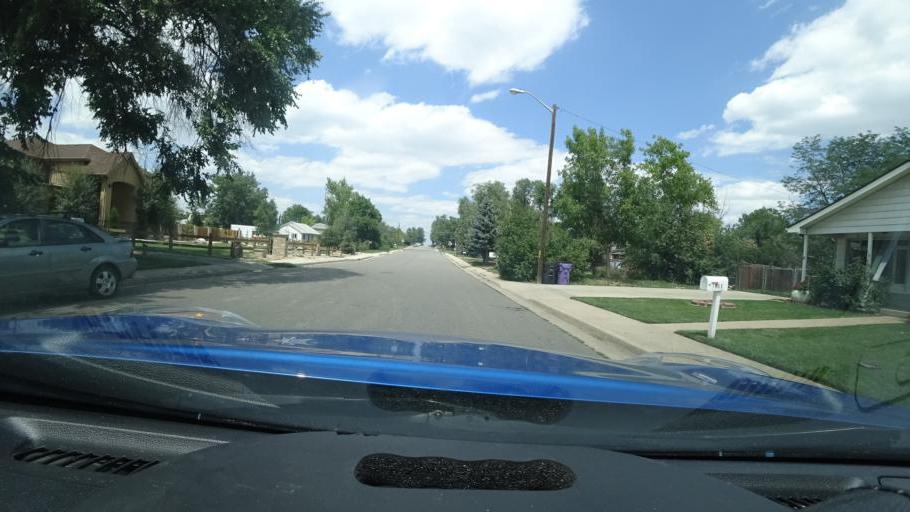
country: US
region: Colorado
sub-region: Arapahoe County
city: Sheridan
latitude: 39.6812
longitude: -105.0180
